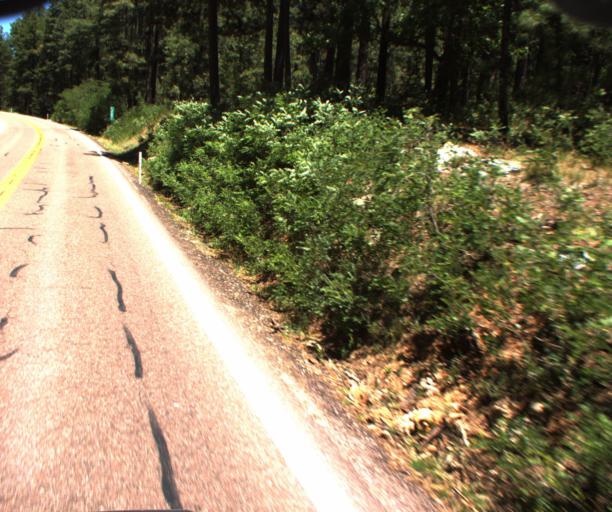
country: US
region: Arizona
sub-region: Gila County
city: Pine
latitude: 34.5106
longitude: -111.3411
